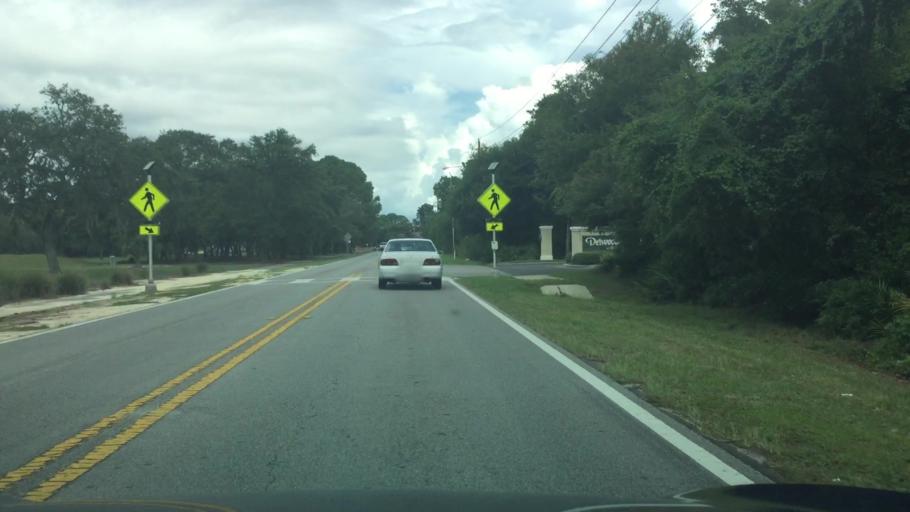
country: US
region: Florida
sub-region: Bay County
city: Upper Grand Lagoon
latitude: 30.1566
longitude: -85.7316
